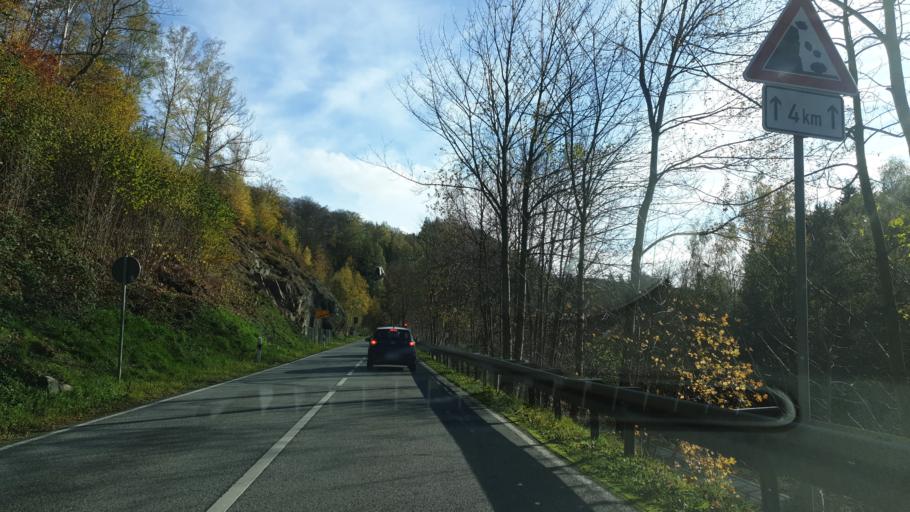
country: DE
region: Saxony
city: Aue
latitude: 50.5775
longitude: 12.6892
